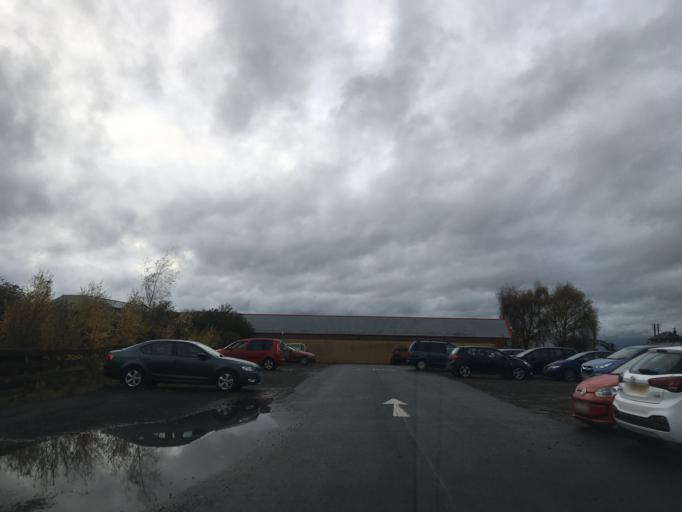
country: GB
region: Scotland
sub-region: Falkirk
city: Bo'ness
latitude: 56.0173
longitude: -3.5999
